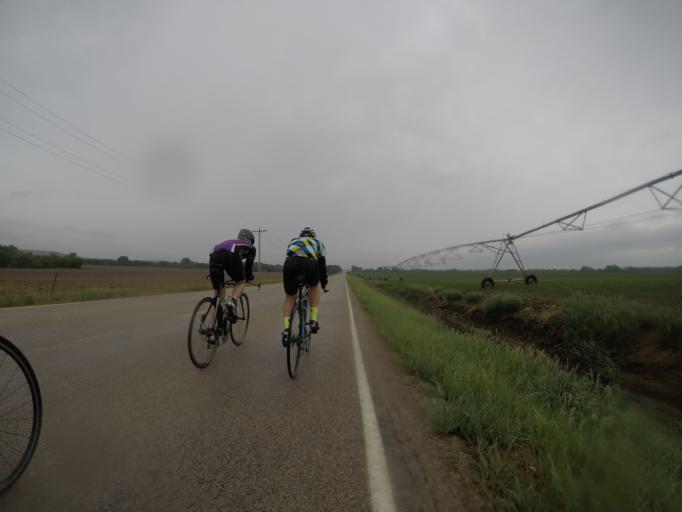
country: US
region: Kansas
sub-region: Pottawatomie County
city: Wamego
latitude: 39.3439
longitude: -96.2212
